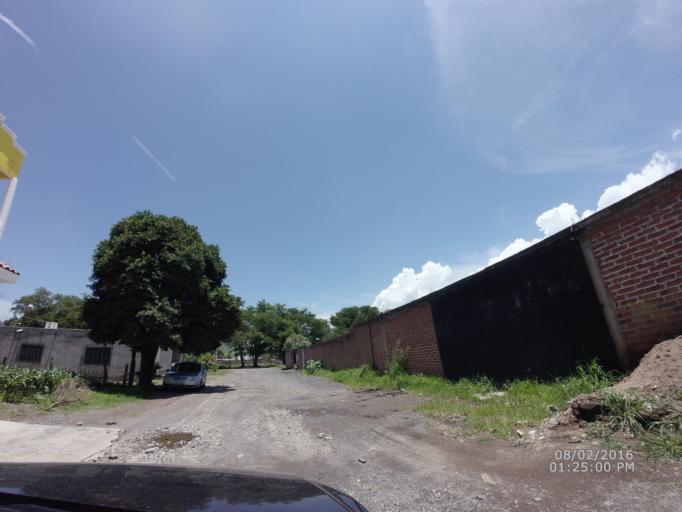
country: MX
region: Nayarit
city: Ixtlan del Rio
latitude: 21.0386
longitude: -104.3766
